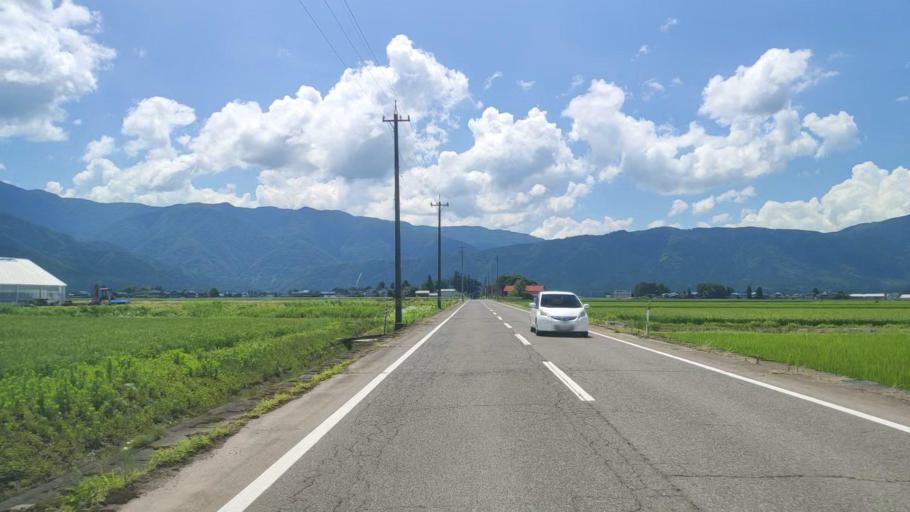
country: JP
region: Fukui
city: Ono
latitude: 35.9669
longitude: 136.5285
